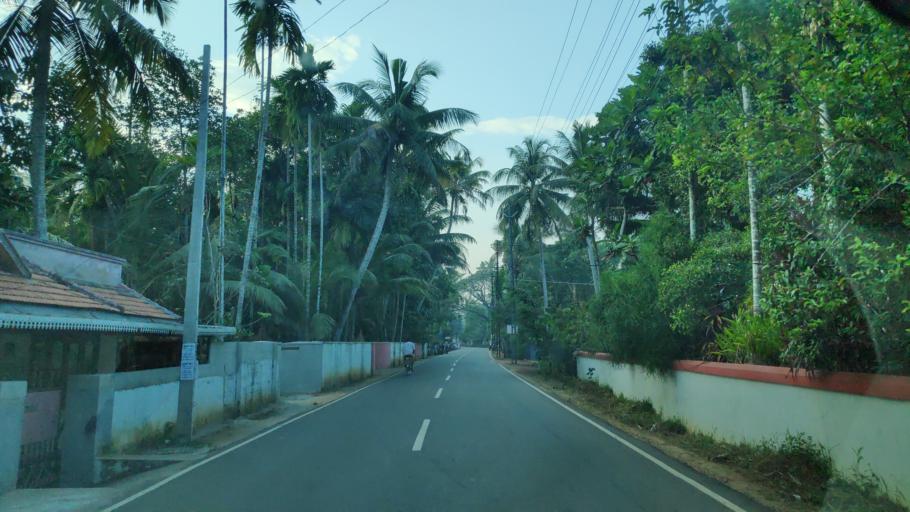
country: IN
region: Kerala
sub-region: Alappuzha
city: Shertallai
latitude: 9.6779
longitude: 76.3776
